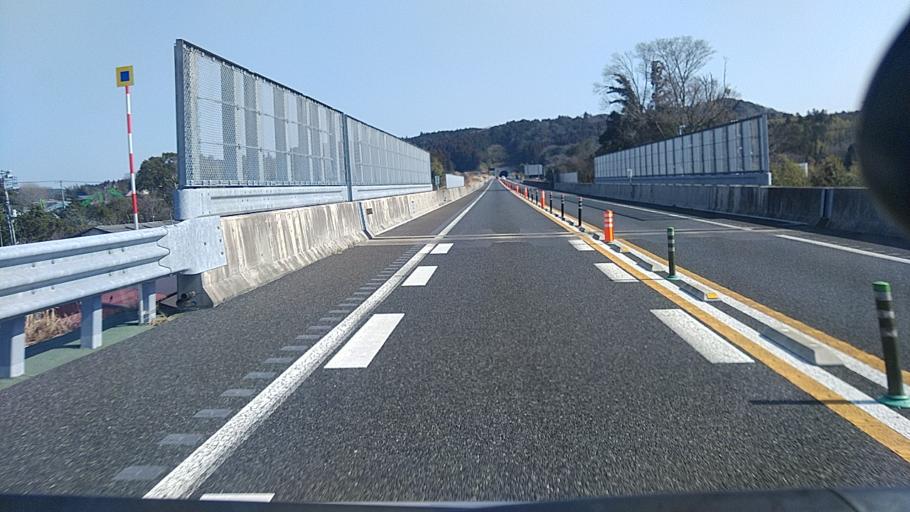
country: JP
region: Chiba
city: Kisarazu
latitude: 35.3592
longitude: 140.0565
